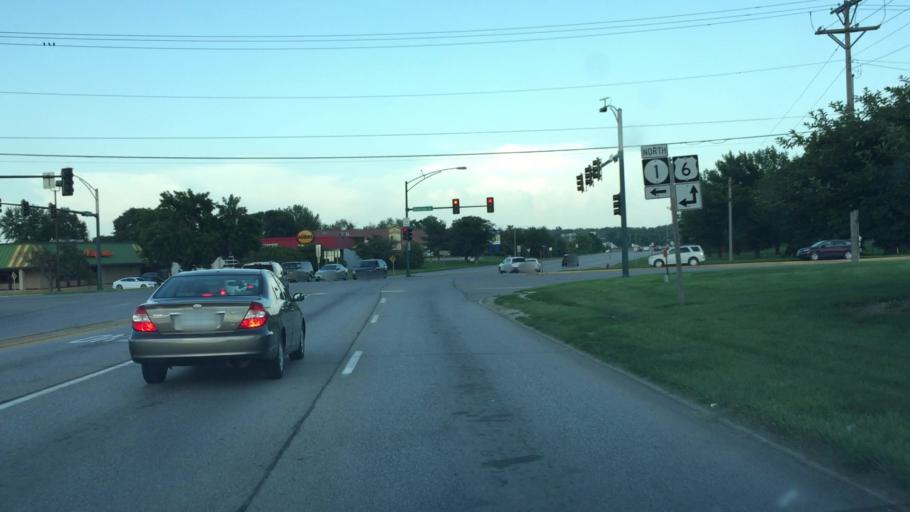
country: US
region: Iowa
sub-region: Johnson County
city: Iowa City
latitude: 41.6474
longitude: -91.5408
